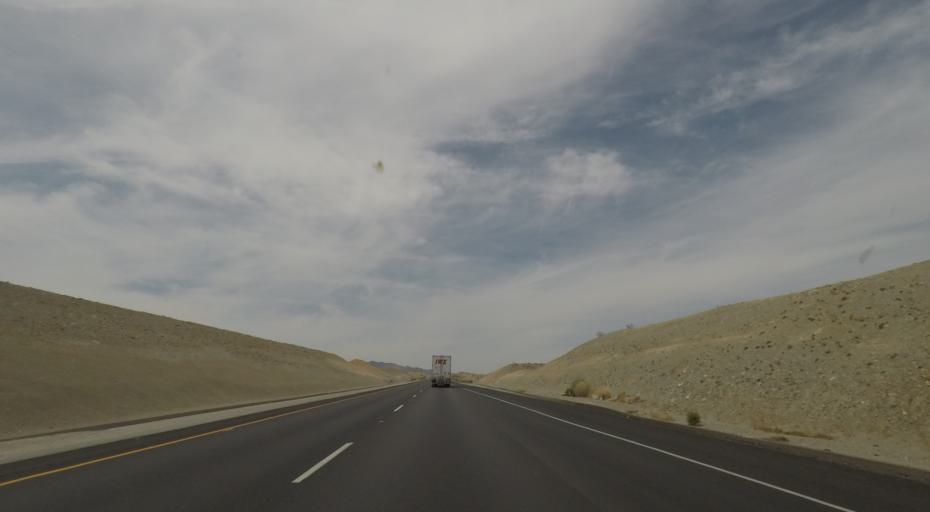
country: US
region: California
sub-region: San Bernardino County
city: Needles
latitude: 34.7176
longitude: -114.5149
